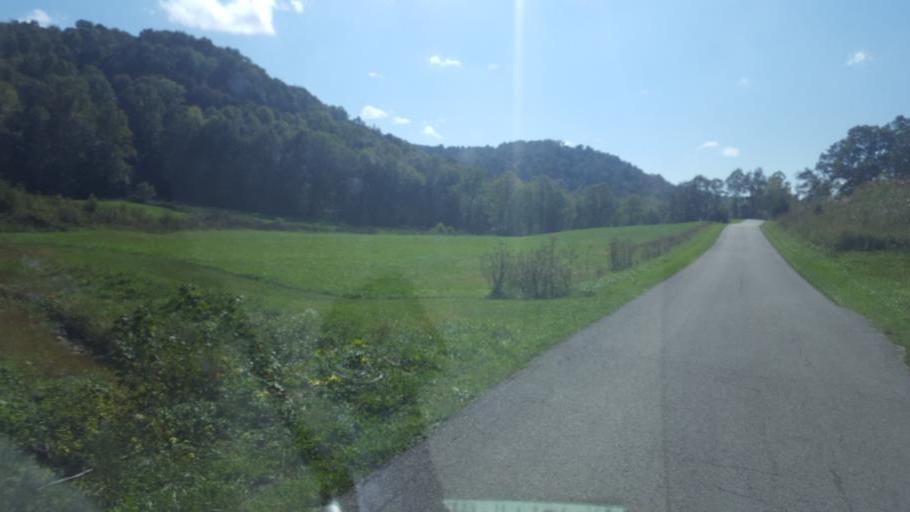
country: US
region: Kentucky
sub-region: Fleming County
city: Flemingsburg
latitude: 38.4512
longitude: -83.5424
